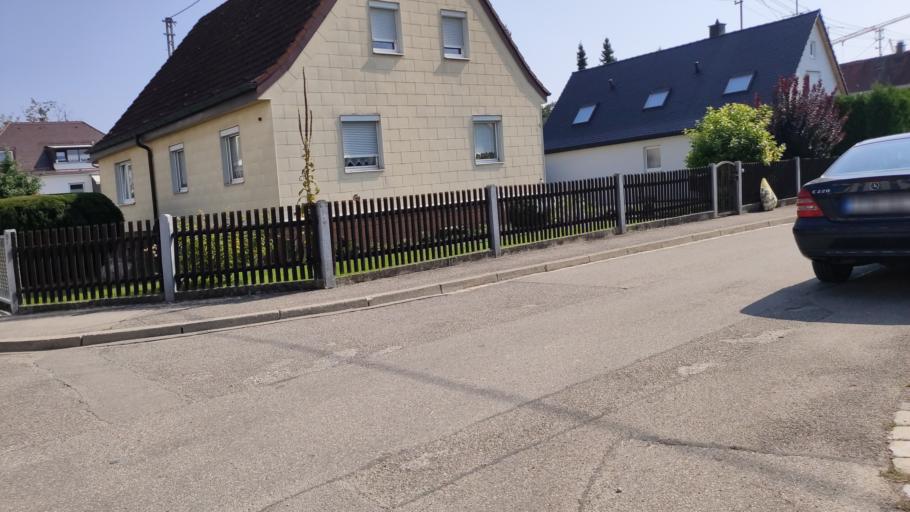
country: DE
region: Bavaria
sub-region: Swabia
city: Bobingen
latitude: 48.2640
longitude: 10.8277
